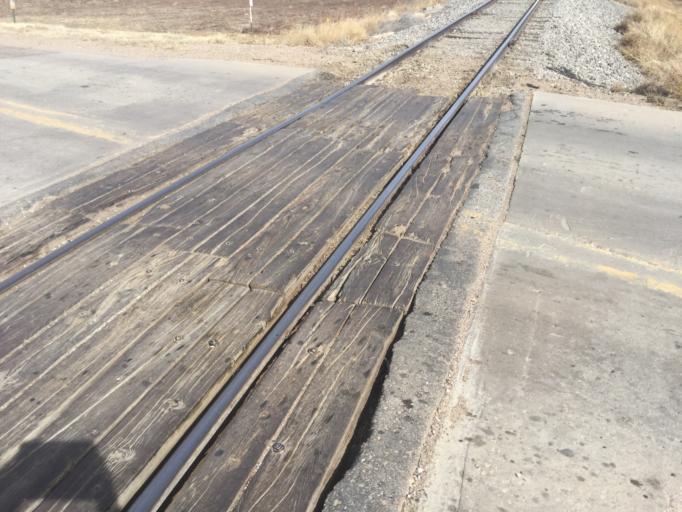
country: US
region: Kansas
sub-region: Haskell County
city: Sublette
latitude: 37.4837
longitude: -100.8390
